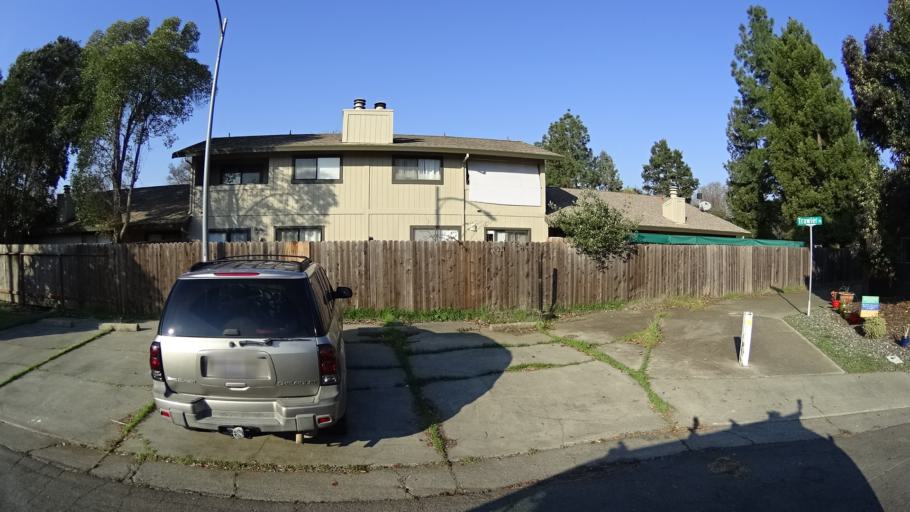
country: US
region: California
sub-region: Yolo County
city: Davis
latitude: 38.5513
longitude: -121.7929
